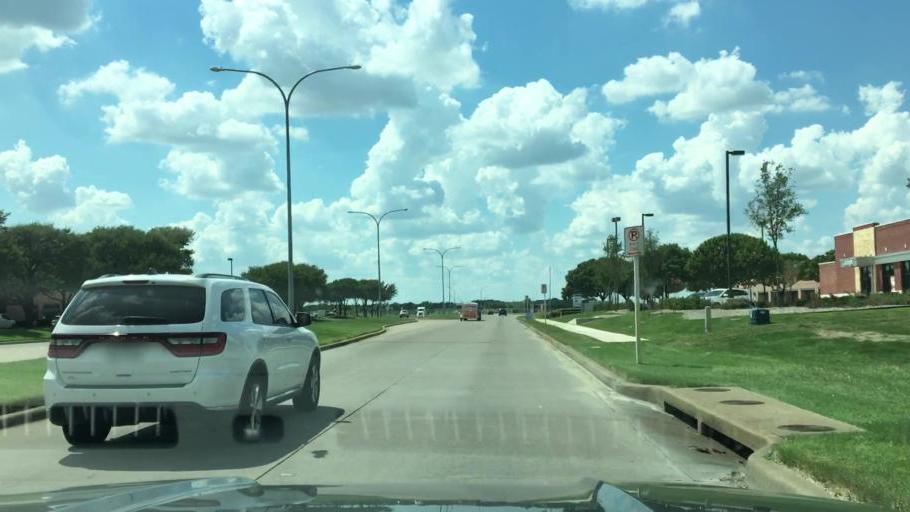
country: US
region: Texas
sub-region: Tarrant County
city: Haslet
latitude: 32.9724
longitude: -97.3099
